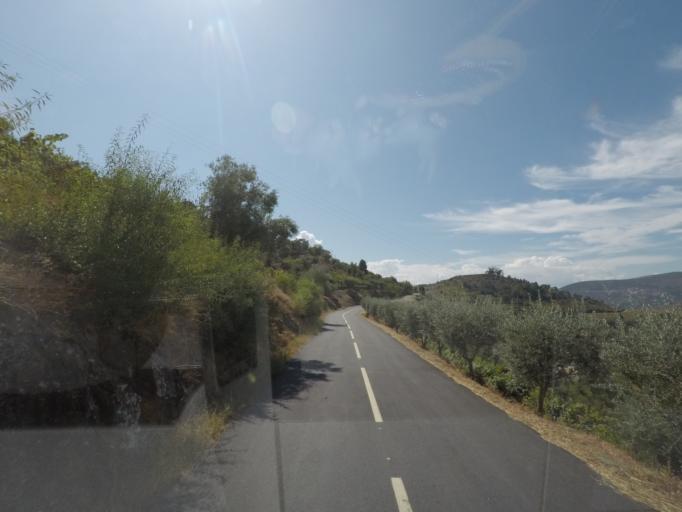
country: PT
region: Vila Real
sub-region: Sabrosa
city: Sabrosa
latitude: 41.2192
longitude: -7.5252
